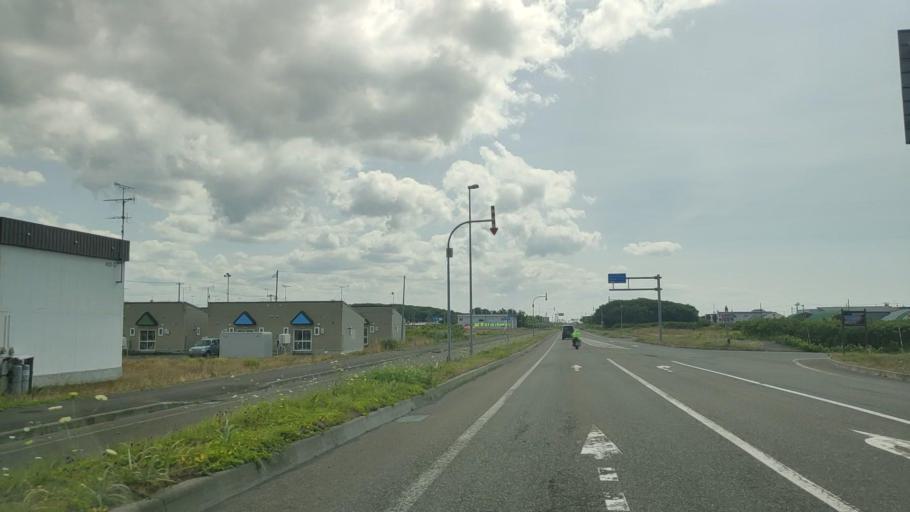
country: JP
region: Hokkaido
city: Makubetsu
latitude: 44.8810
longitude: 141.7496
